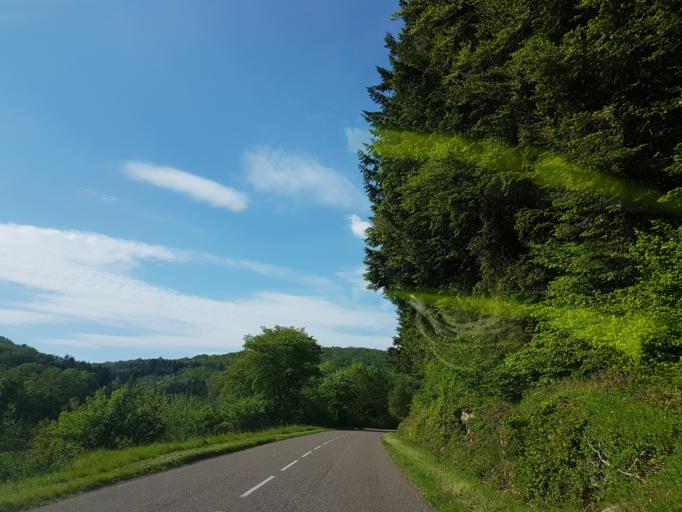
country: FR
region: Franche-Comte
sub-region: Departement de la Haute-Saone
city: Froideconche
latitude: 47.8534
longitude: 6.4797
